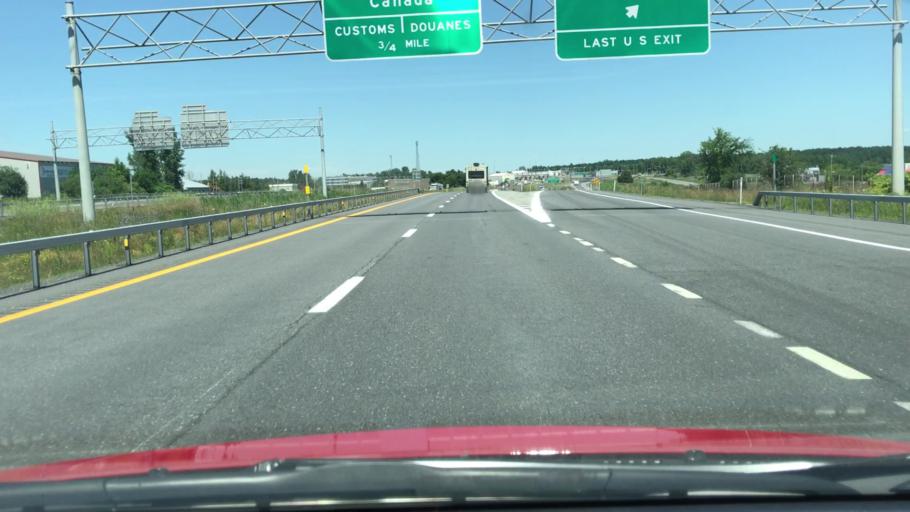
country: US
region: New York
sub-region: Clinton County
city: Champlain
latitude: 44.9964
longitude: -73.4556
